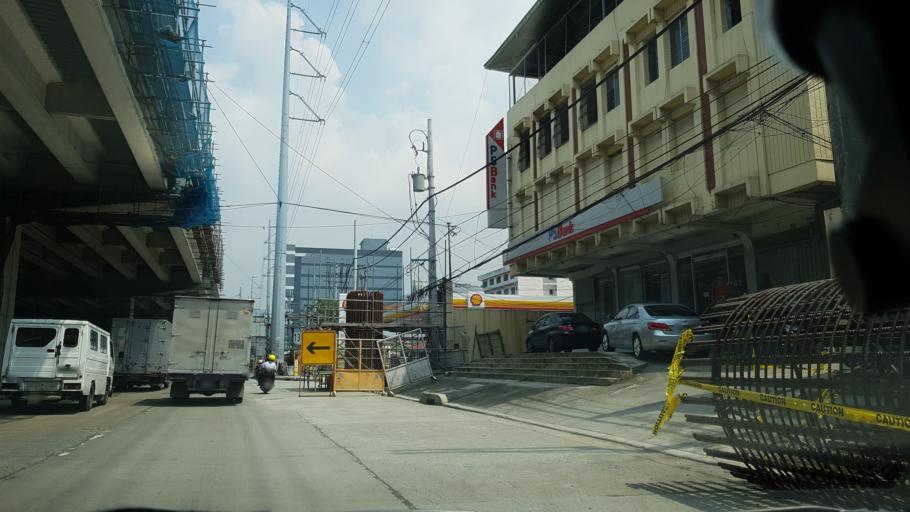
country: PH
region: Metro Manila
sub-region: San Juan
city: San Juan
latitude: 14.6106
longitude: 121.0171
